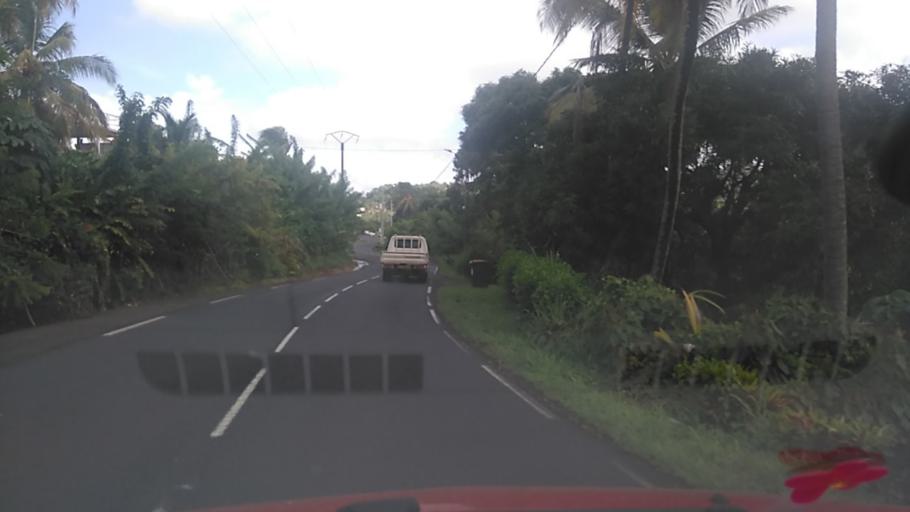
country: MQ
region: Martinique
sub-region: Martinique
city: Le Francois
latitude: 14.5990
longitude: -60.9311
